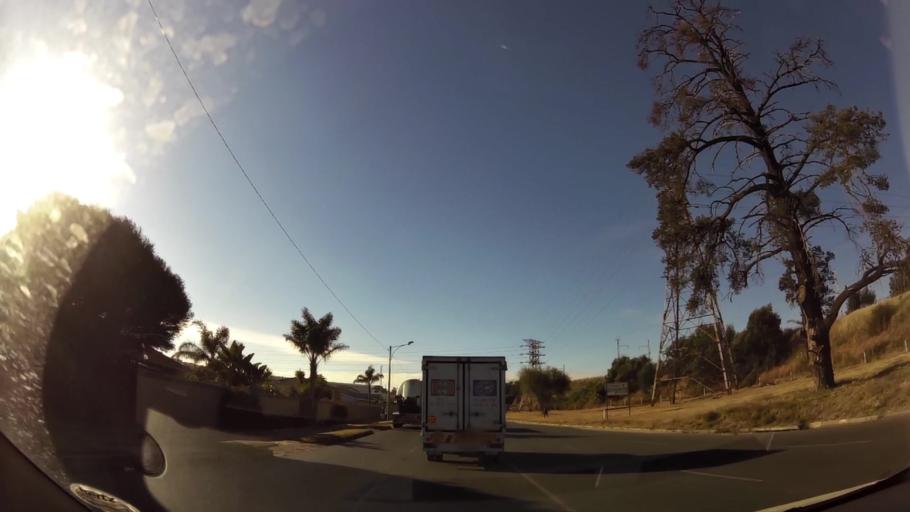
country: ZA
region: Gauteng
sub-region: West Rand District Municipality
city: Krugersdorp
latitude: -26.1173
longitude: 27.8021
